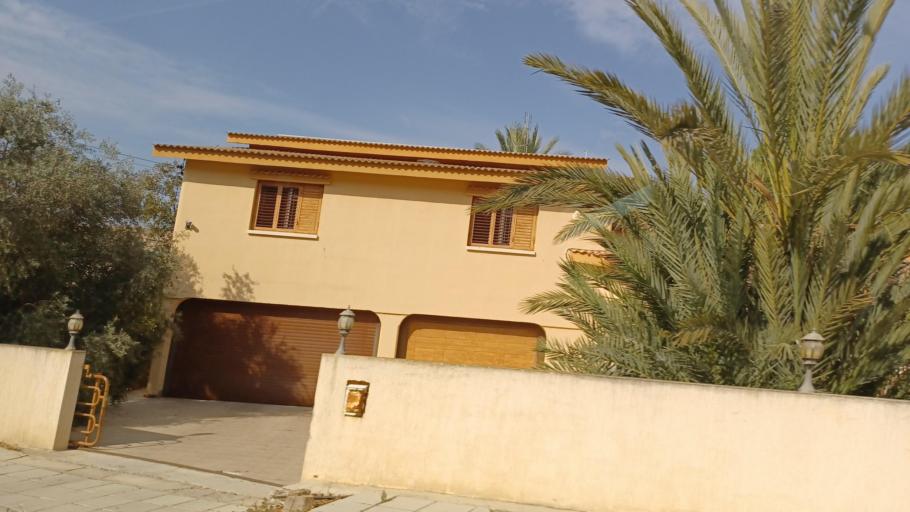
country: CY
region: Lefkosia
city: Lympia
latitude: 34.9939
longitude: 33.4628
